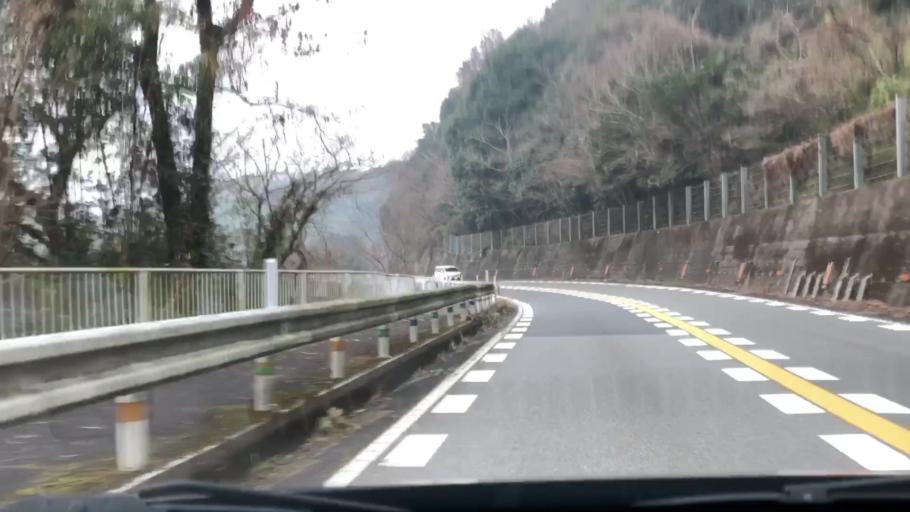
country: JP
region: Oita
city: Usuki
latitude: 33.0255
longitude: 131.6944
